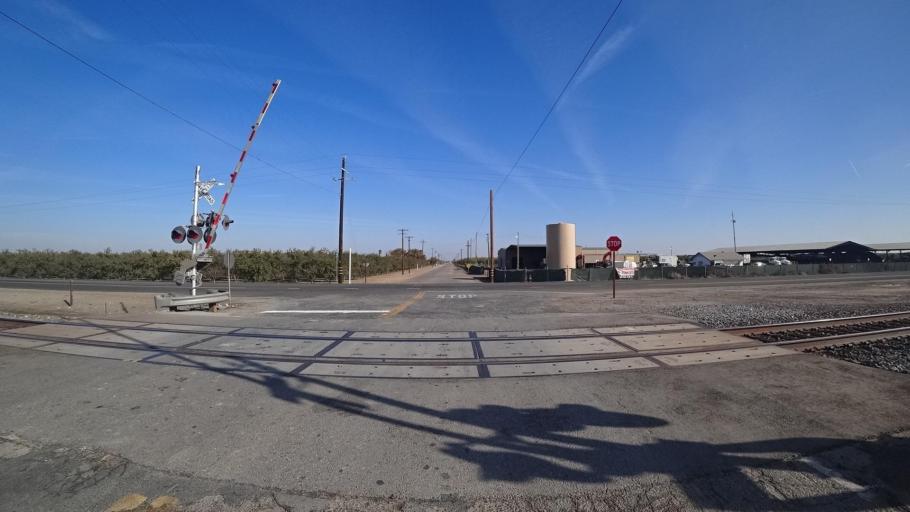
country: US
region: California
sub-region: Kern County
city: McFarland
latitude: 35.7031
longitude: -119.3308
